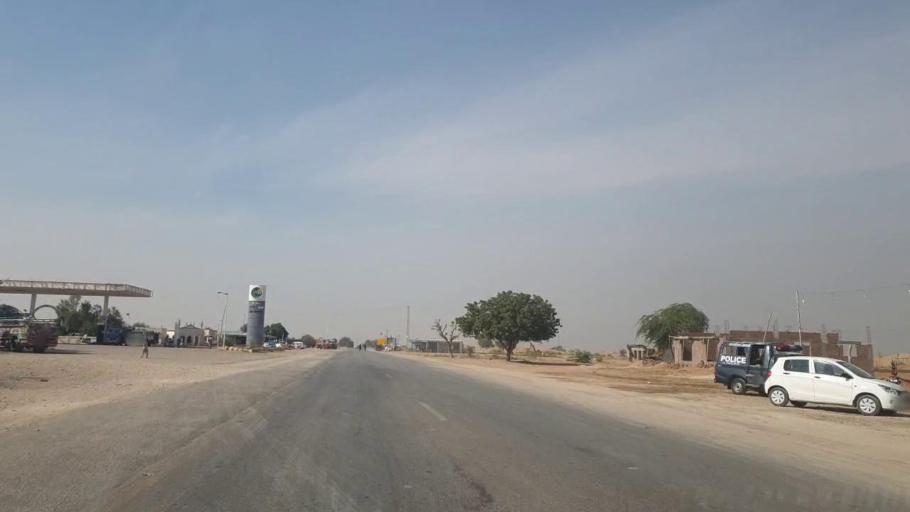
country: PK
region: Sindh
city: Sann
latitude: 26.0273
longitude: 68.1262
